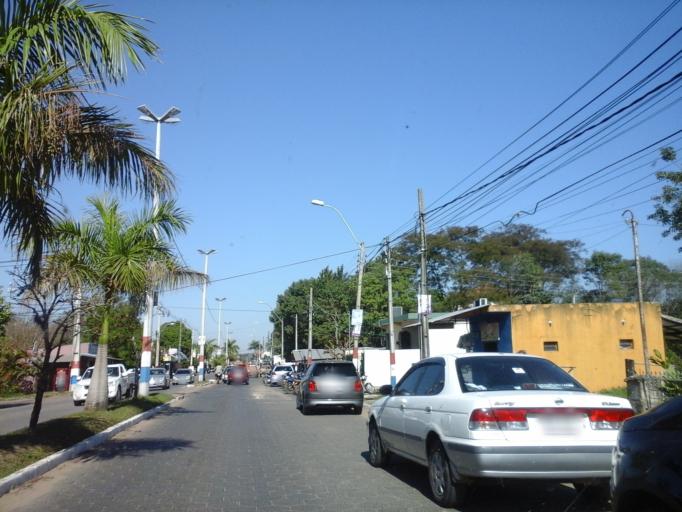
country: PY
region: Neembucu
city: Pilar
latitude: -26.8676
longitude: -58.3018
